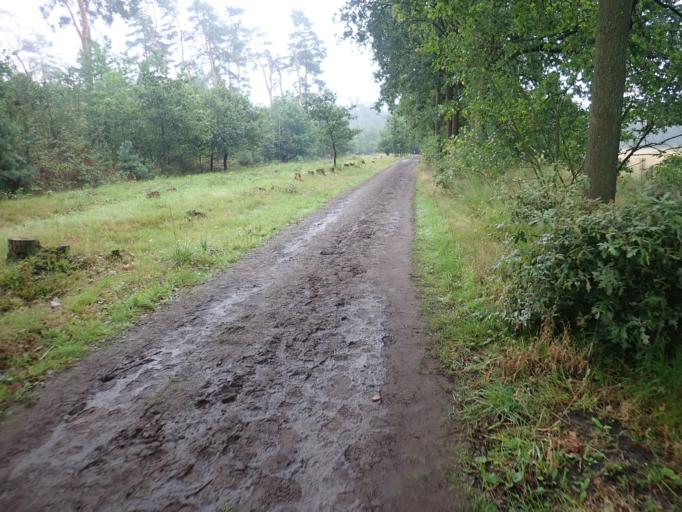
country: BE
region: Flanders
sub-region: Provincie Antwerpen
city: Lille
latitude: 51.2794
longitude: 4.8111
